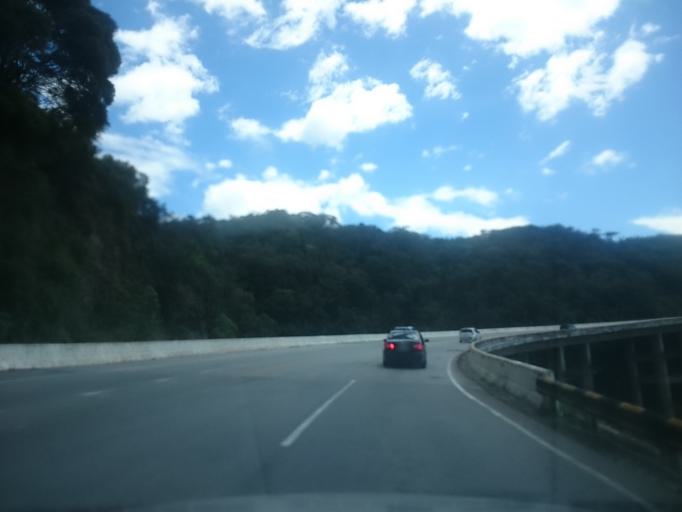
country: BR
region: Santa Catarina
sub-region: Anitapolis
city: Anitapolis
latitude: -27.6834
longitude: -49.1075
